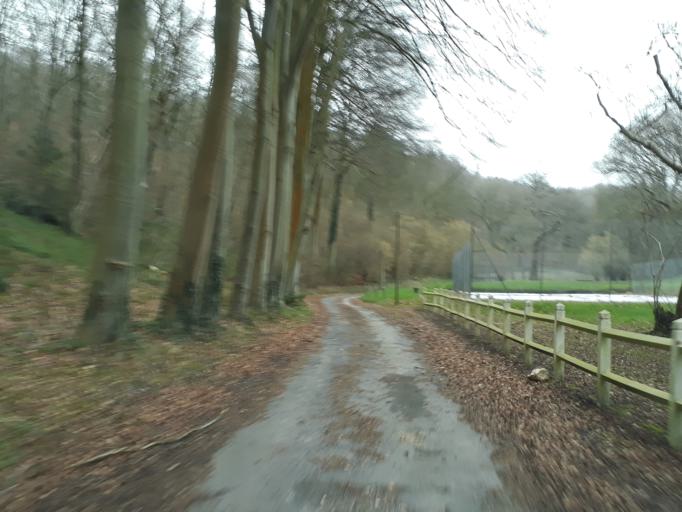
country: FR
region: Haute-Normandie
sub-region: Departement de la Seine-Maritime
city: Yport
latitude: 49.7308
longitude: 0.2952
